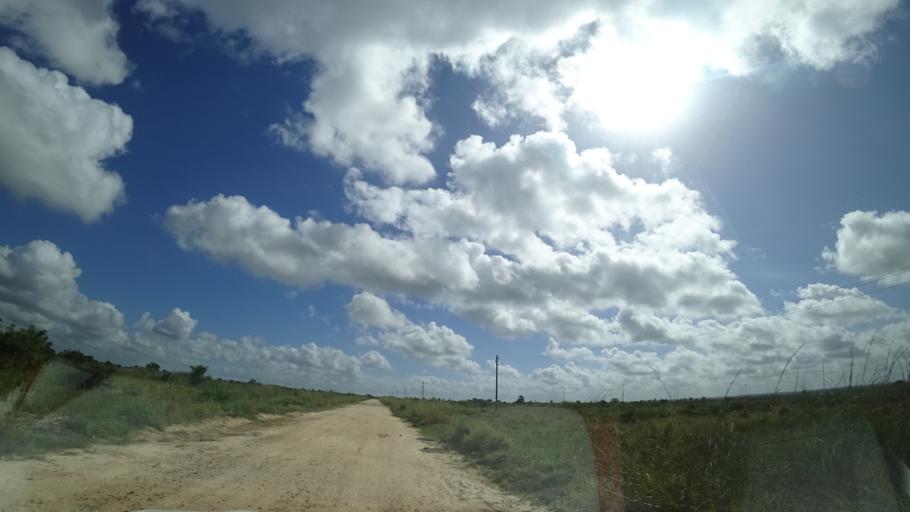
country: MZ
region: Sofala
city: Dondo
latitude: -19.4505
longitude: 34.5625
